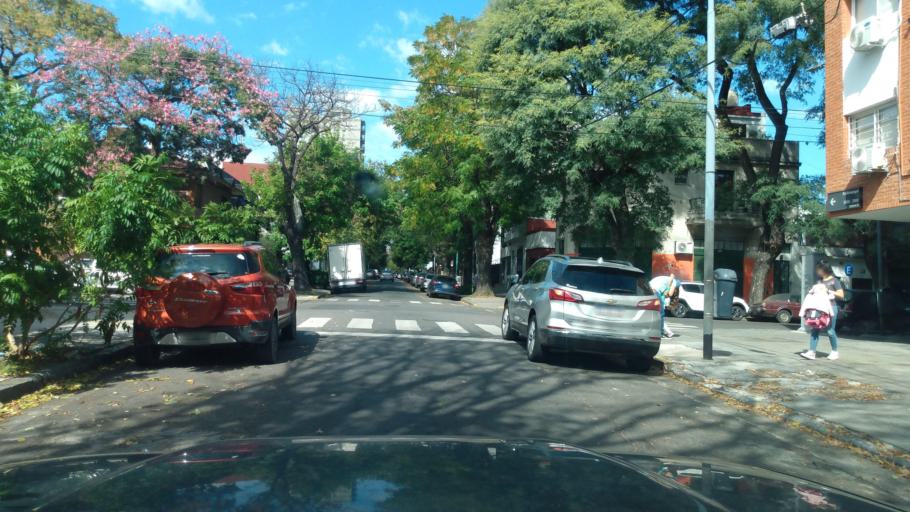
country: AR
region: Buenos Aires
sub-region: Partido de General San Martin
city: General San Martin
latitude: -34.5730
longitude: -58.4926
